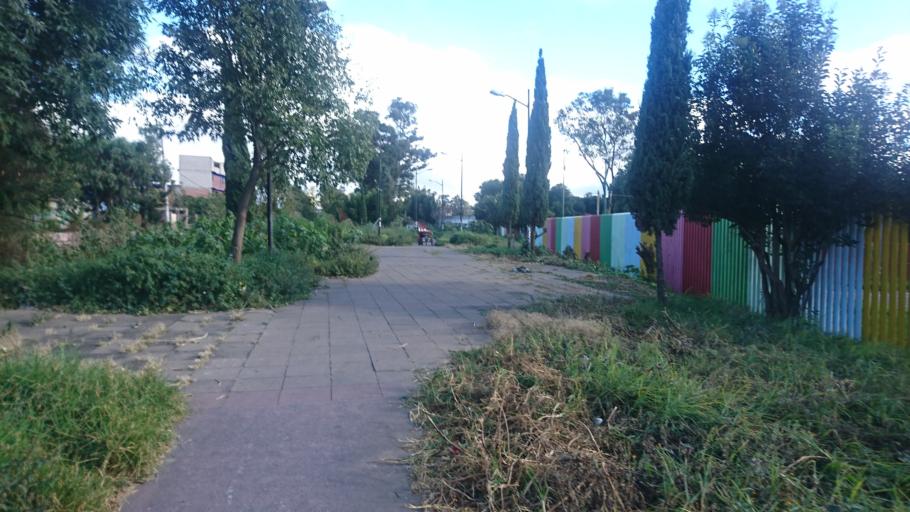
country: MX
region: Mexico City
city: Iztapalapa
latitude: 19.3255
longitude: -99.1052
